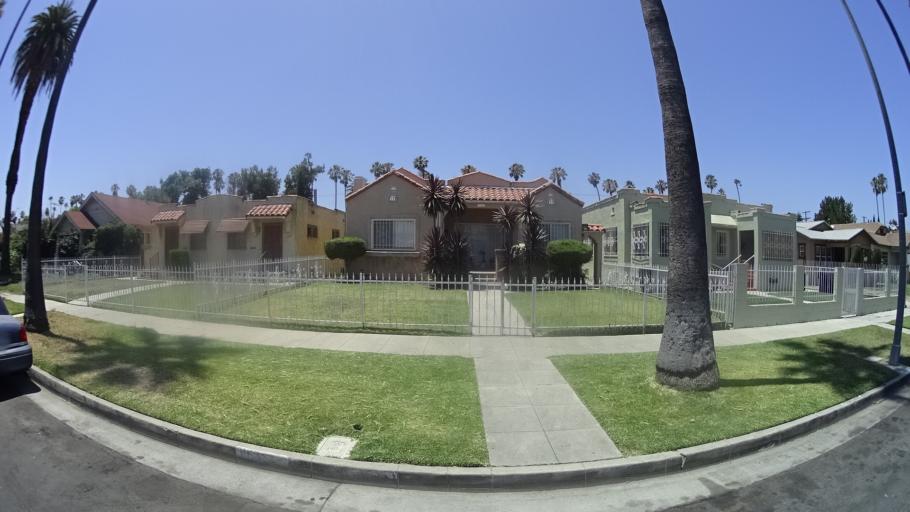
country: US
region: California
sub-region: Los Angeles County
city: View Park-Windsor Hills
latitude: 33.9956
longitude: -118.3126
